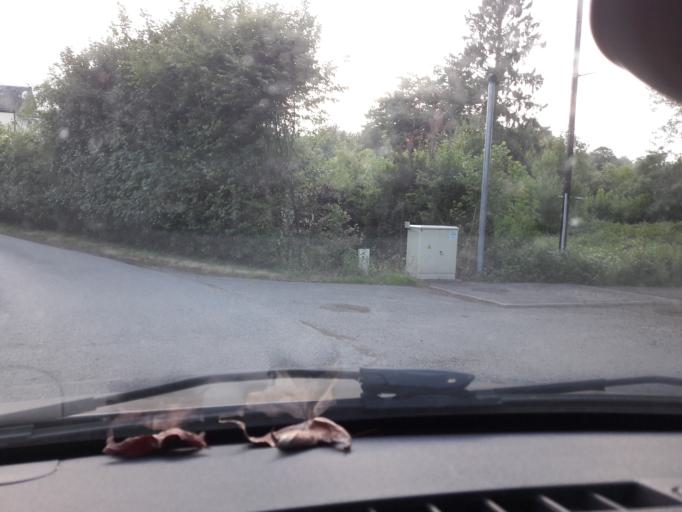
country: BE
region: Wallonia
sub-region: Province du Hainaut
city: Merbes-le-Chateau
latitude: 50.2647
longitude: 4.1808
